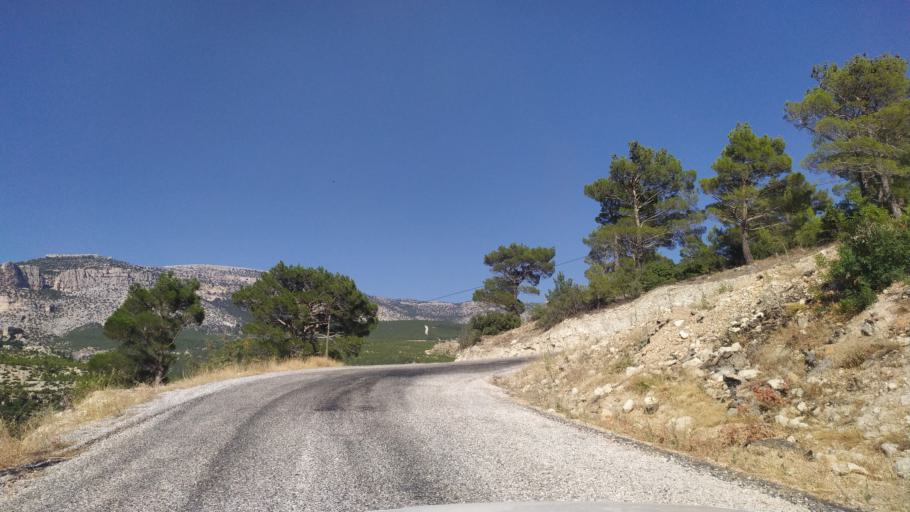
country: TR
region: Mersin
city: Mut
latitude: 36.7032
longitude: 33.4744
